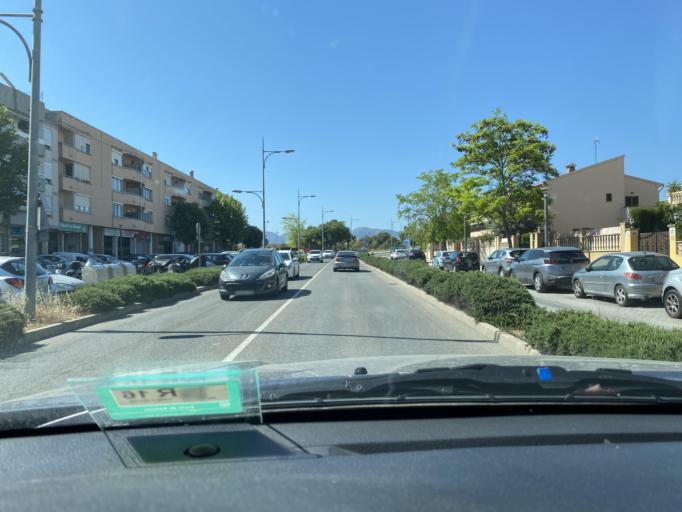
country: ES
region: Balearic Islands
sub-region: Illes Balears
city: Palma
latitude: 39.6039
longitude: 2.6870
